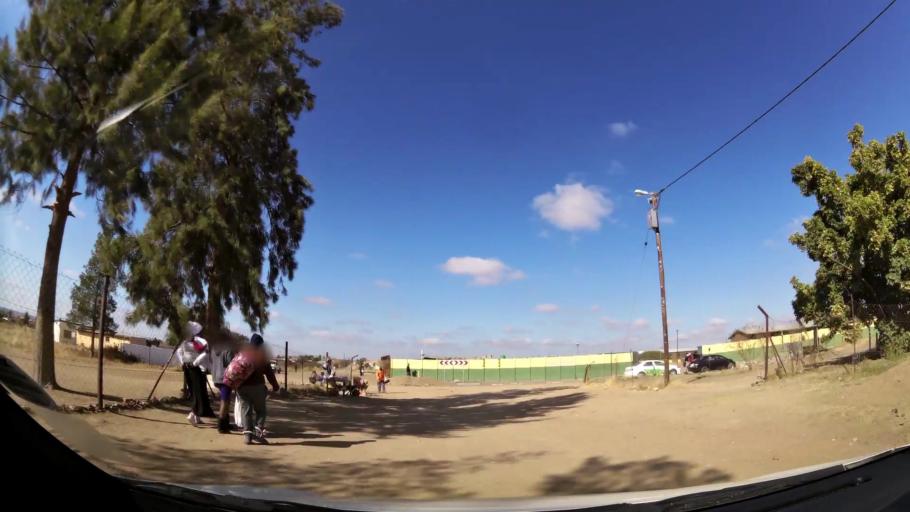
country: ZA
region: Limpopo
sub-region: Capricorn District Municipality
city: Polokwane
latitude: -23.8585
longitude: 29.3807
